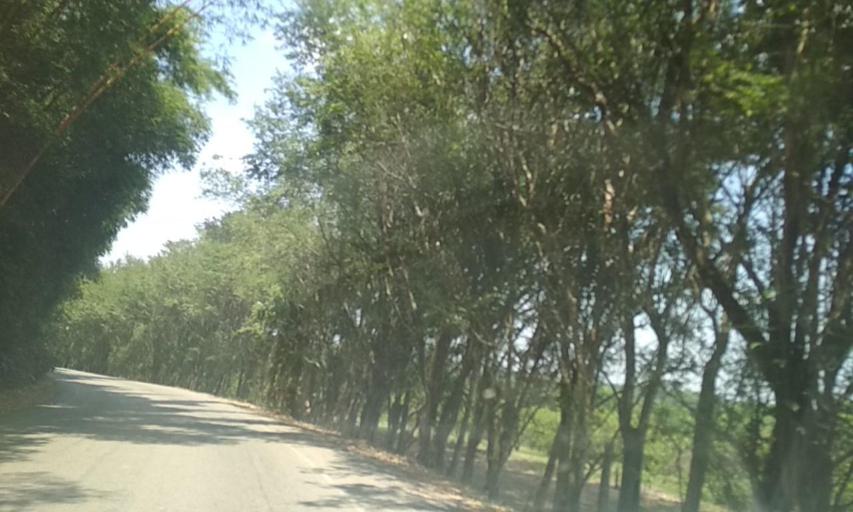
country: MX
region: Tabasco
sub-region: Huimanguillo
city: Paso de la Mina 2da. Seccion (Barrial)
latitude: 17.7775
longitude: -93.6389
